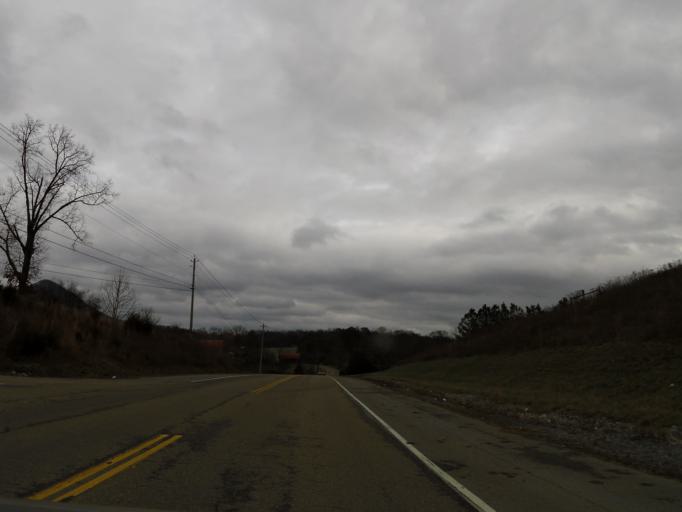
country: US
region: Tennessee
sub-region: Grainger County
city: Blaine
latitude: 36.1521
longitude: -83.7518
